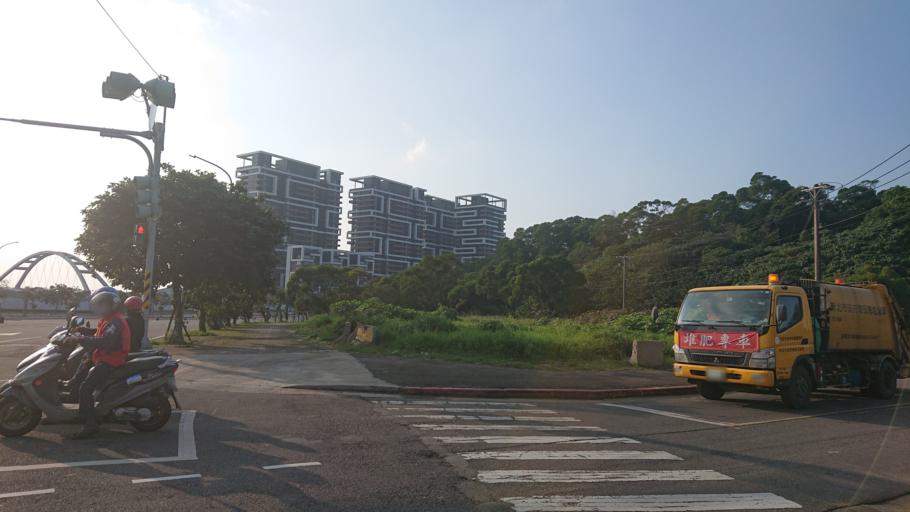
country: TW
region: Taipei
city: Taipei
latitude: 25.1915
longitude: 121.4250
